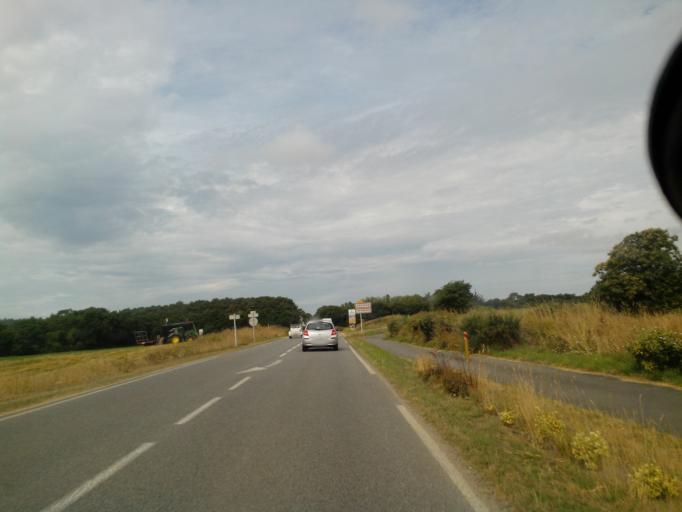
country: FR
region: Brittany
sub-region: Departement du Morbihan
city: Erdeven
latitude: 47.6412
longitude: -3.1392
